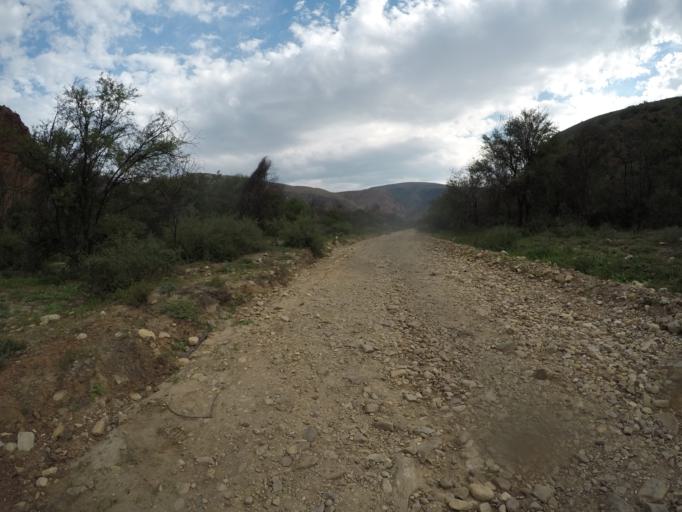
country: ZA
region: Eastern Cape
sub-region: Cacadu District Municipality
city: Kareedouw
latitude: -33.6026
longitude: 24.2067
